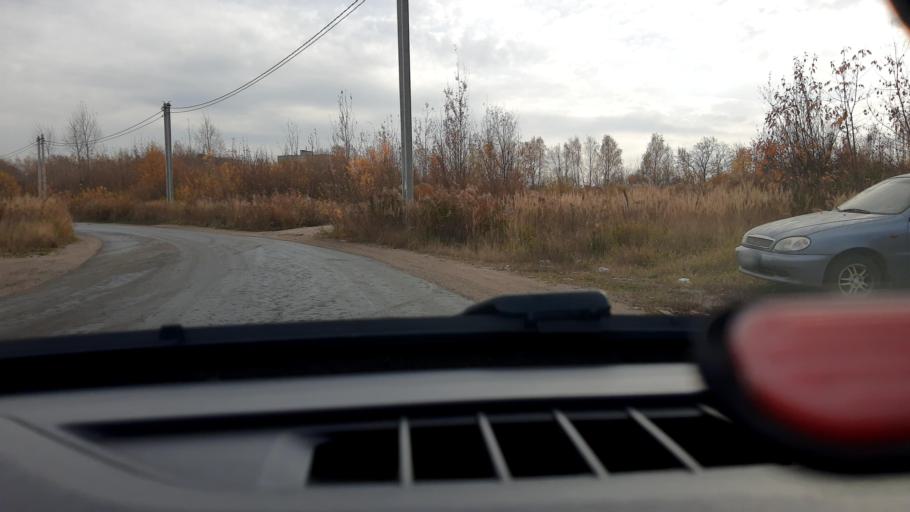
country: RU
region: Nizjnij Novgorod
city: Gorbatovka
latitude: 56.3165
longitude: 43.8464
